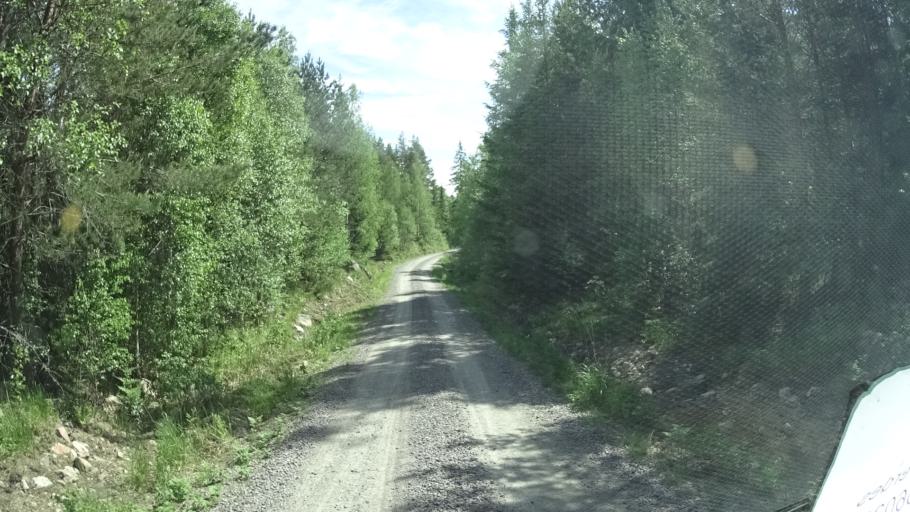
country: SE
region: OEstergoetland
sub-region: Finspangs Kommun
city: Finspang
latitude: 58.7855
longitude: 15.9009
